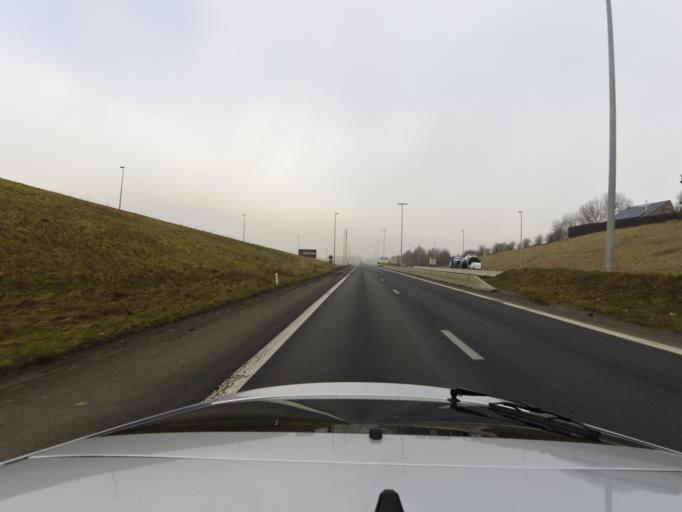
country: BE
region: Flanders
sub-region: Provincie West-Vlaanderen
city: Kortrijk
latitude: 50.7819
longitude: 3.2438
